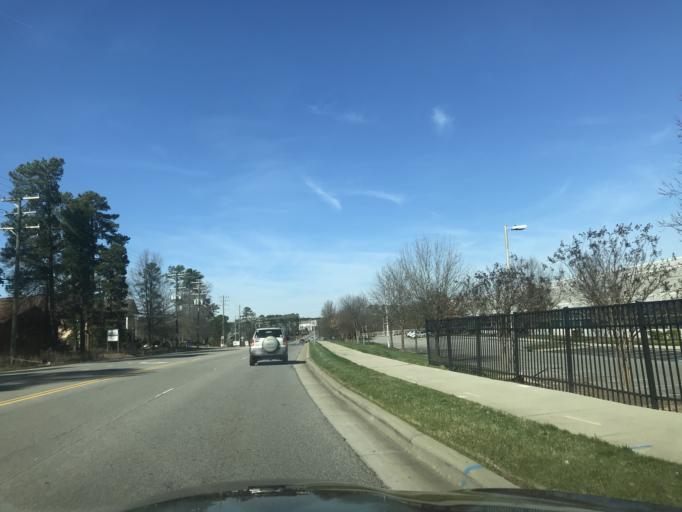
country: US
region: North Carolina
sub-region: Wake County
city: Morrisville
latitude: 35.8691
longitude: -78.8505
